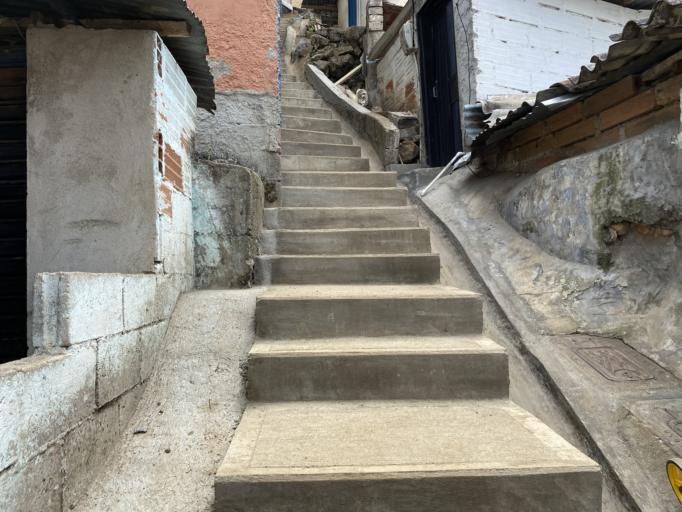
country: CO
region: Antioquia
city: Medellin
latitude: 6.2795
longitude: -75.5443
